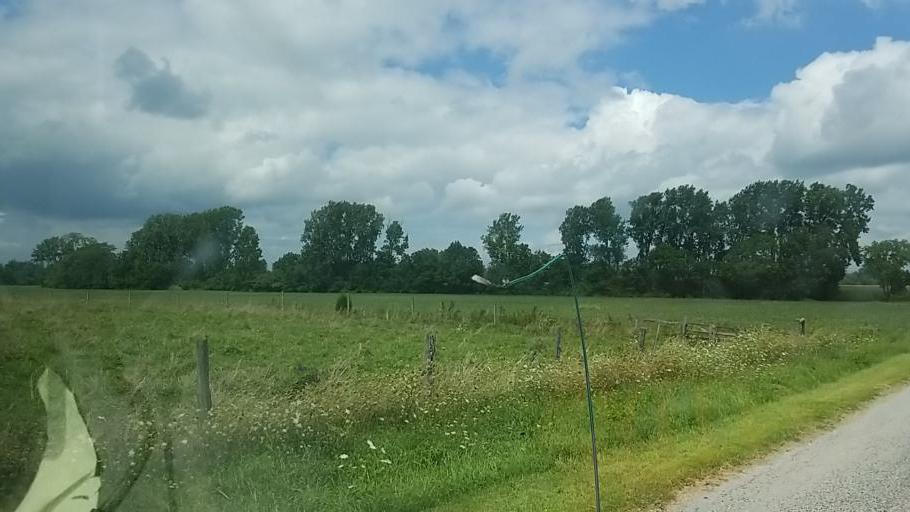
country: US
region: Ohio
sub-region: Clark County
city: South Charleston
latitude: 39.8220
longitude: -83.7209
